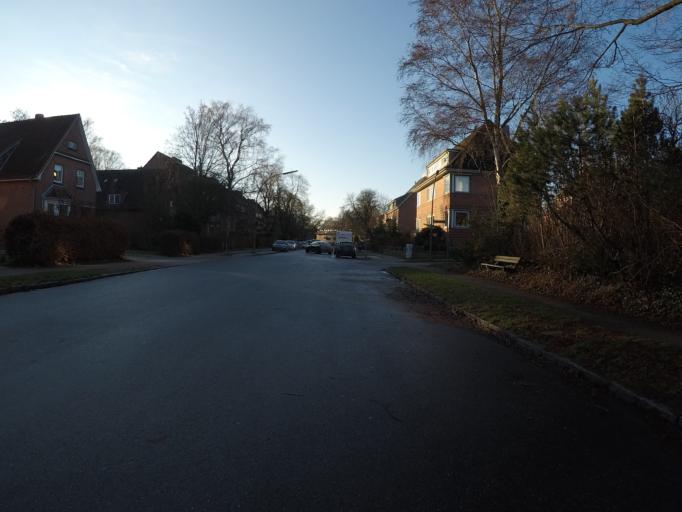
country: DE
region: Hamburg
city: Fuhlsbuettel
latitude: 53.6423
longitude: 10.0215
